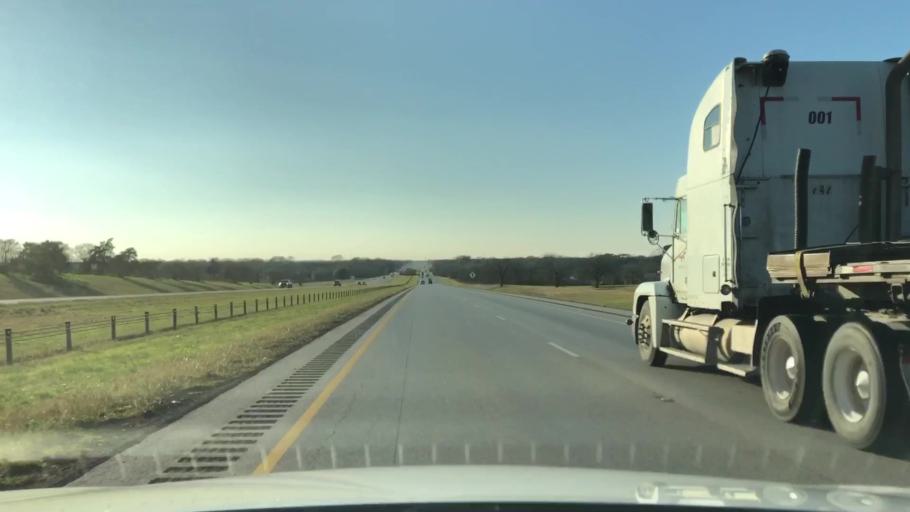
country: US
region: Texas
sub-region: Fayette County
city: Flatonia
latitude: 29.6921
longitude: -97.1763
